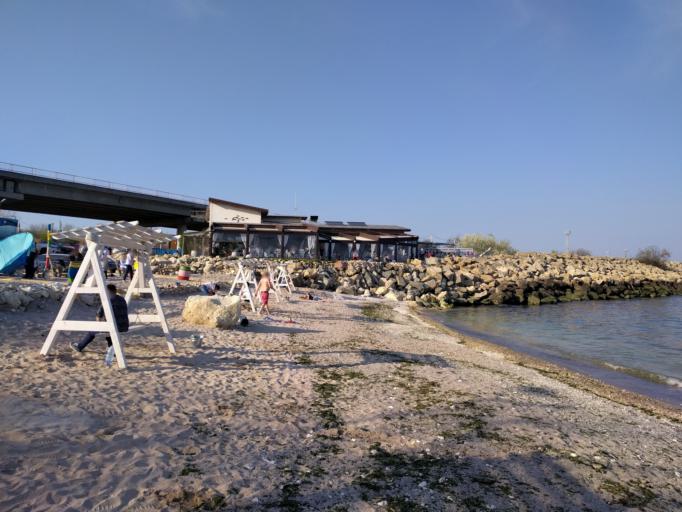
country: RO
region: Constanta
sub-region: Oras Eforie
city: Eforie Nord
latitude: 44.0838
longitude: 28.6433
